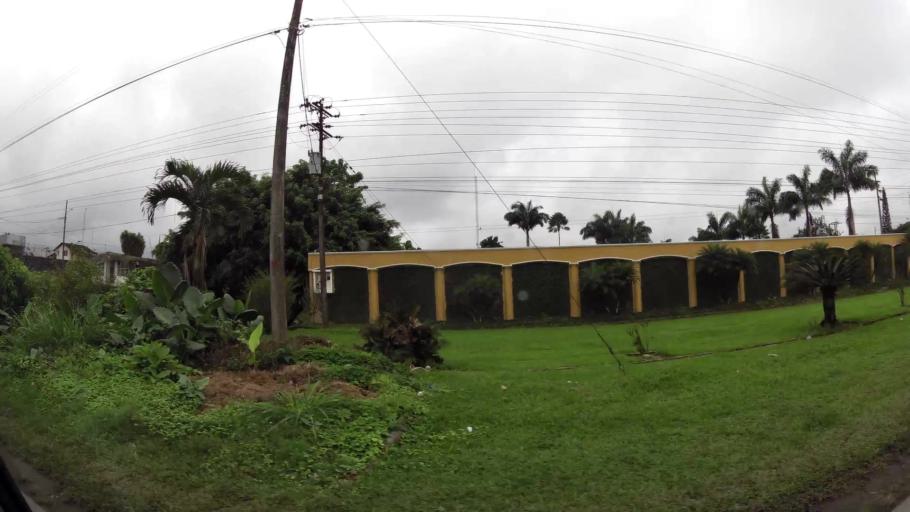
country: EC
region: Santo Domingo de los Tsachilas
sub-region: Canton Santo Domingo de los Colorados
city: Santo Domingo de los Colorados
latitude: -0.2507
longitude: -79.1399
